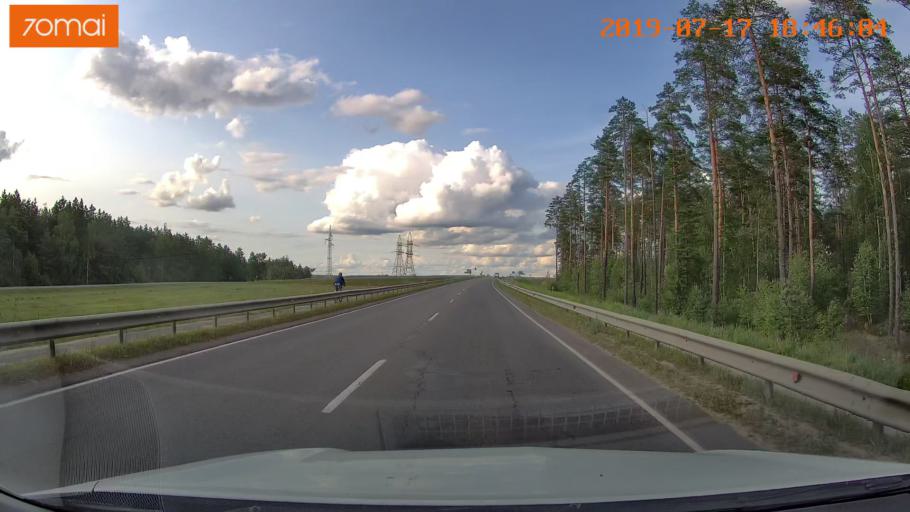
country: BY
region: Mogilev
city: Asipovichy
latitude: 53.3317
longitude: 28.6621
